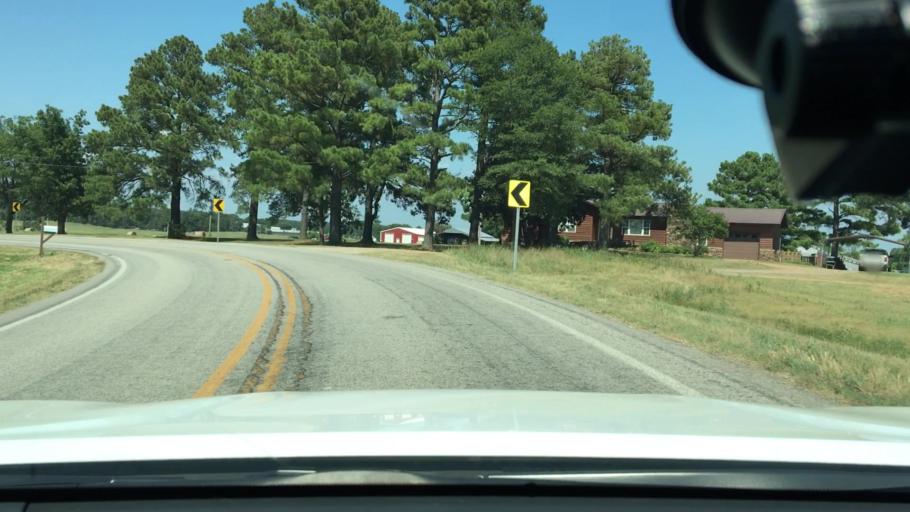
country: US
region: Arkansas
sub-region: Johnson County
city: Coal Hill
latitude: 35.3477
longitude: -93.5891
